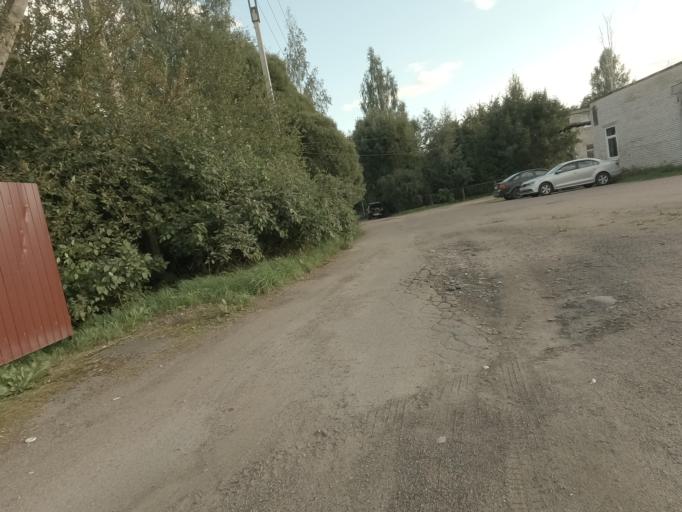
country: RU
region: Leningrad
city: Mga
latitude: 59.7517
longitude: 31.0348
